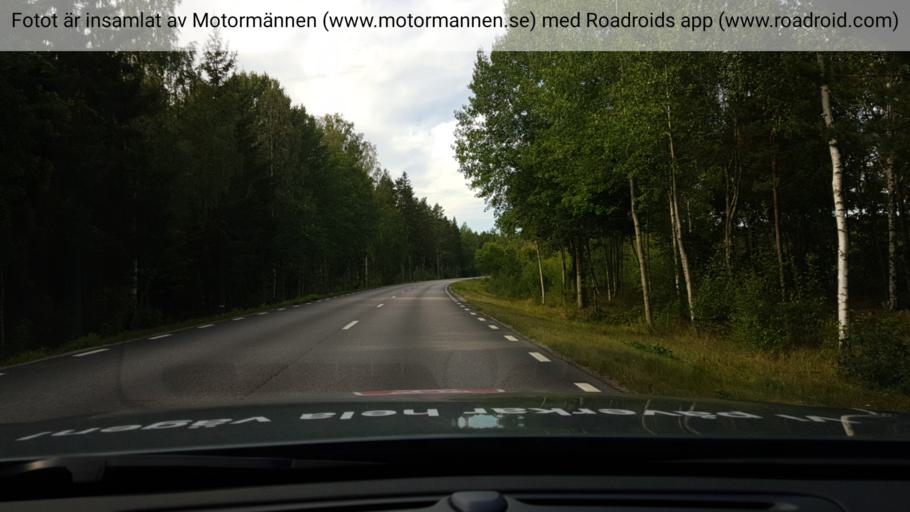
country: SE
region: Gaevleborg
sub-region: Gavle Kommun
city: Hedesunda
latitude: 60.2943
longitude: 16.9079
